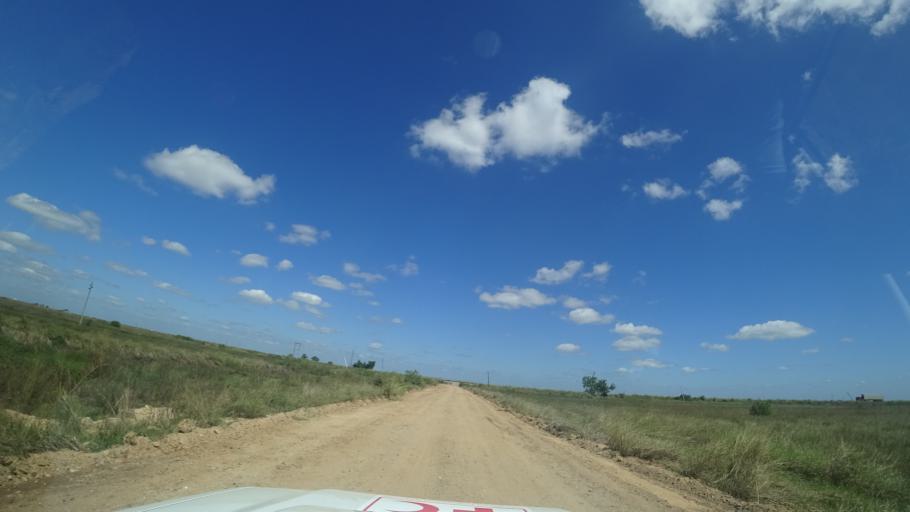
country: MZ
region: Sofala
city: Dondo
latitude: -19.4644
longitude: 34.5610
